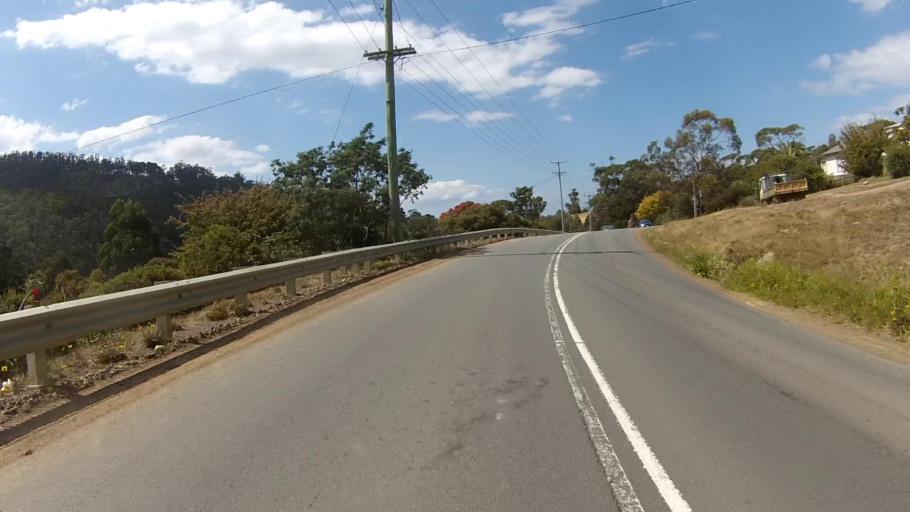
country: AU
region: Tasmania
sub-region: Clarence
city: Cambridge
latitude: -42.8389
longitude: 147.4260
